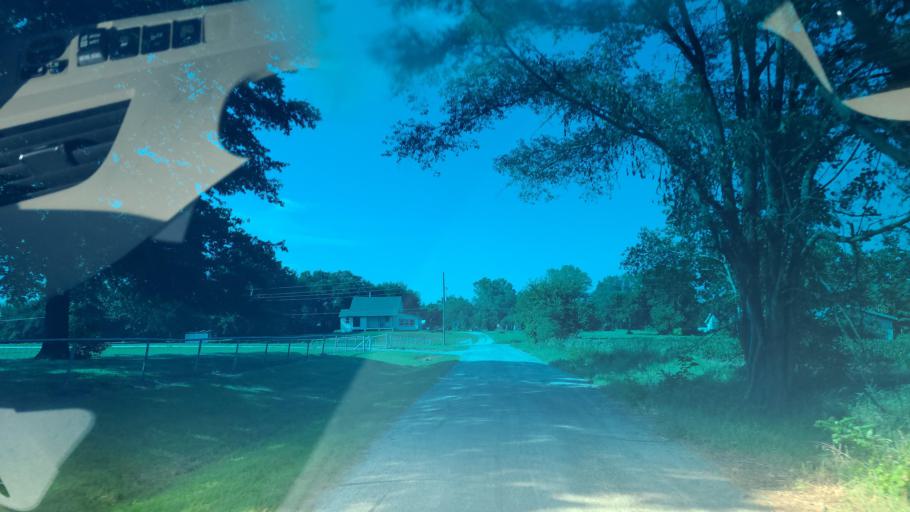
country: US
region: Kansas
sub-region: Douglas County
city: Lawrence
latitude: 38.9813
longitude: -95.2168
